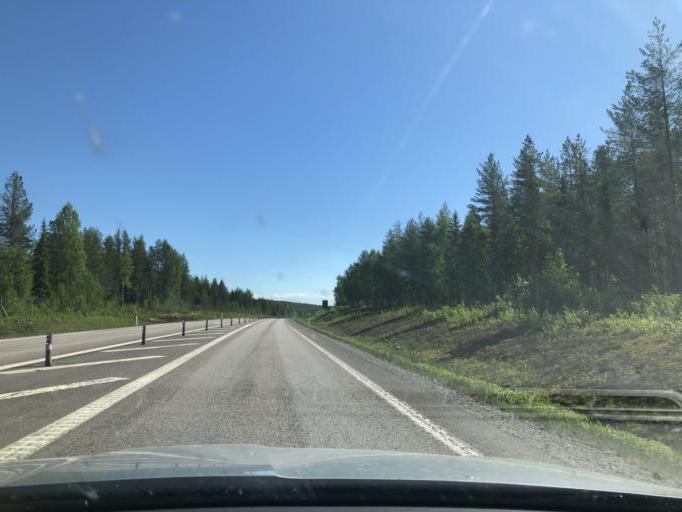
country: SE
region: Norrbotten
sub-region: Kalix Kommun
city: Toere
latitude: 65.9176
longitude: 22.7612
